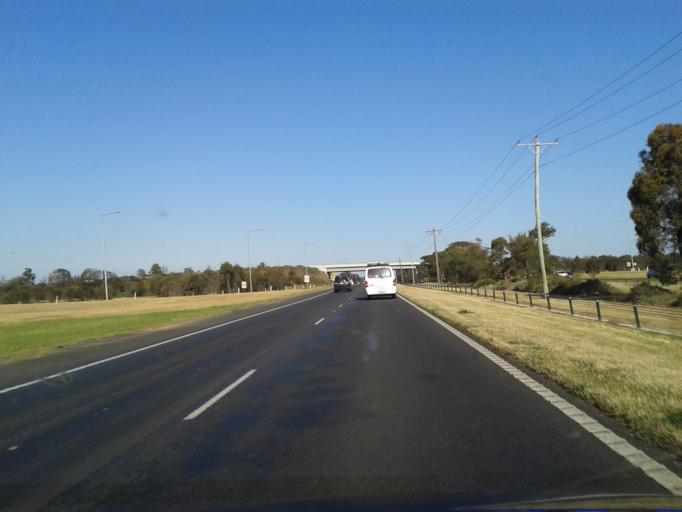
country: AU
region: Victoria
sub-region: Melton
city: Rockbank
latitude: -37.7440
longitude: 144.6977
